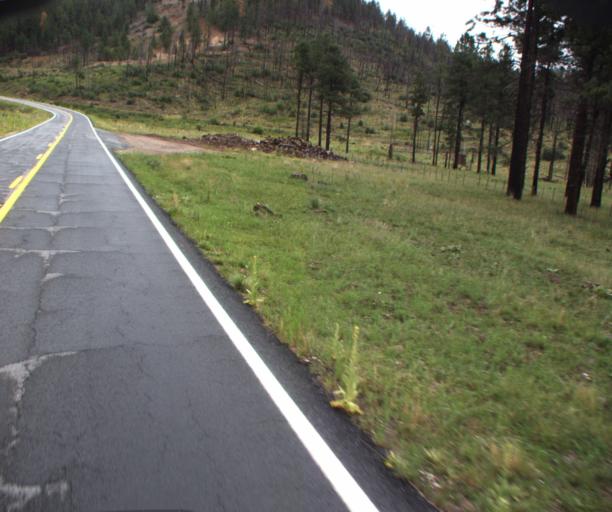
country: US
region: Arizona
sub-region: Apache County
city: Eagar
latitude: 33.8030
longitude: -109.1544
